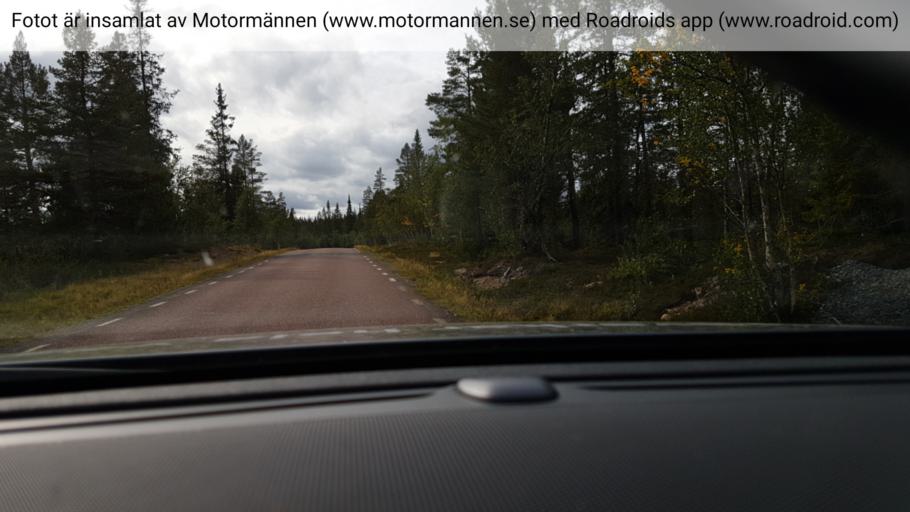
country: NO
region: Hedmark
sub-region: Trysil
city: Innbygda
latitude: 61.6840
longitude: 12.5212
